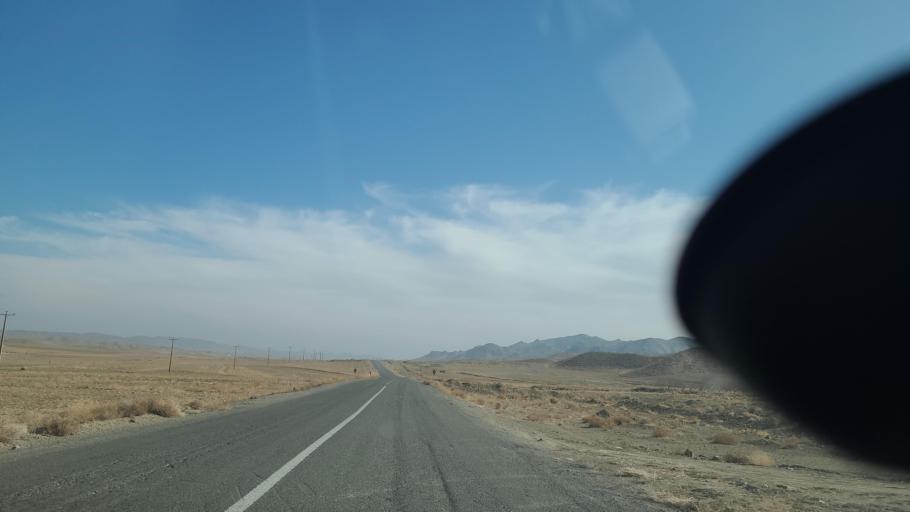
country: IR
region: Razavi Khorasan
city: Fariman
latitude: 35.5875
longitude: 59.6400
